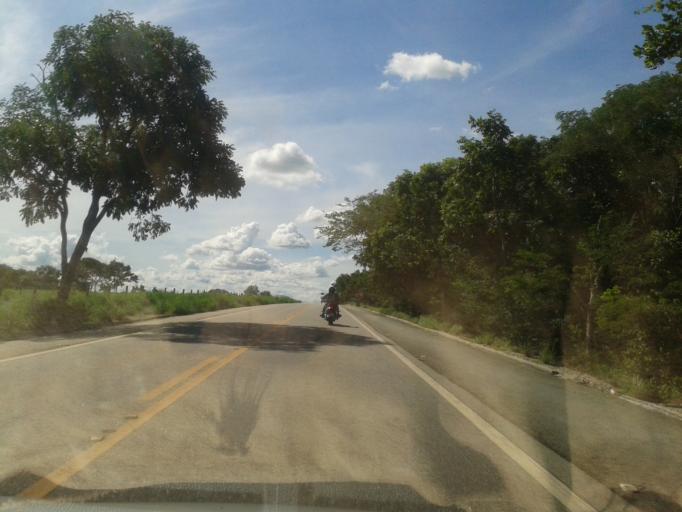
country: BR
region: Goias
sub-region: Itapirapua
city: Itapirapua
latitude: -15.2998
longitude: -50.4536
